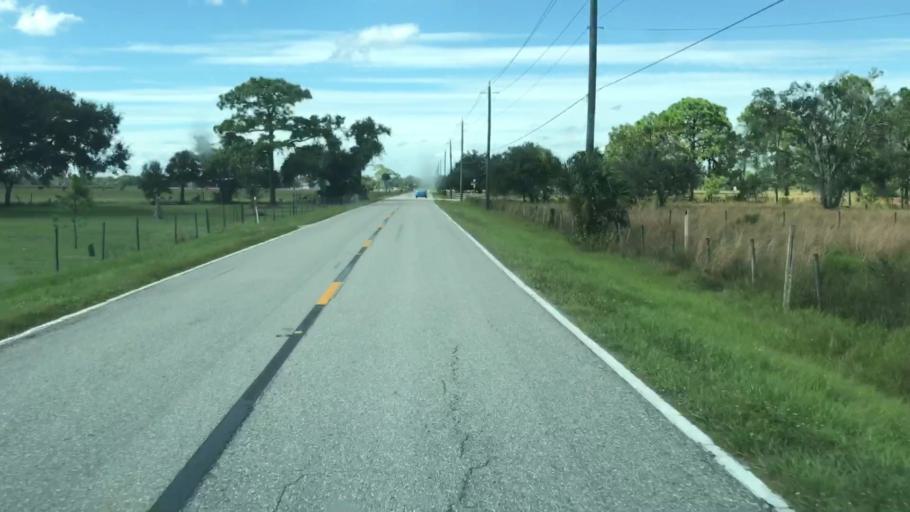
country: US
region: Florida
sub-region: Lee County
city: Alva
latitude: 26.7207
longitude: -81.6146
